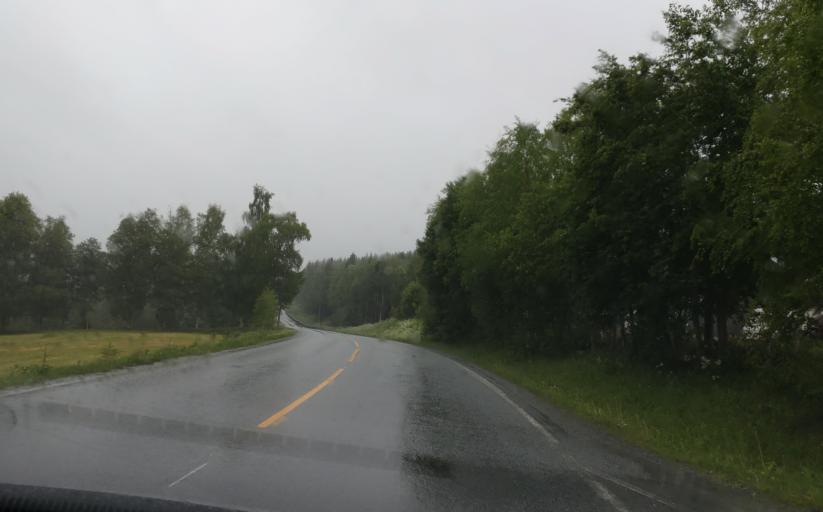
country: NO
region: Nord-Trondelag
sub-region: Stjordal
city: Stjordalshalsen
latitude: 63.4027
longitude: 10.9436
